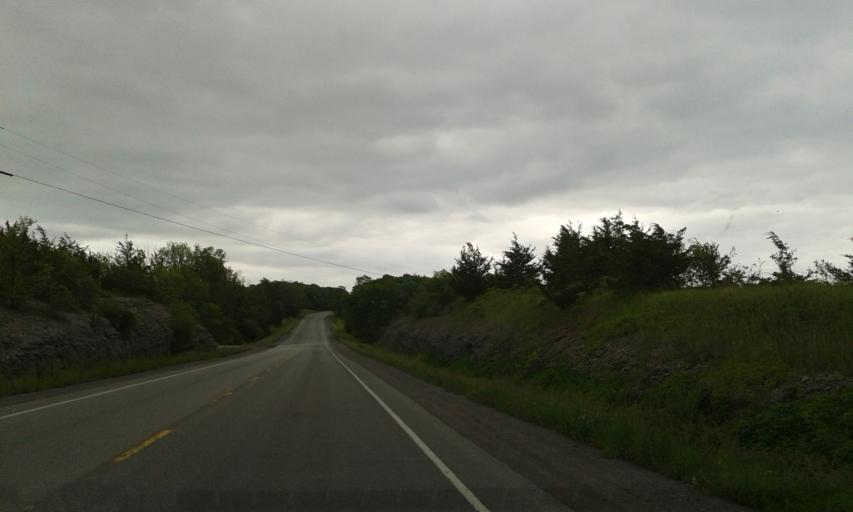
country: CA
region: Ontario
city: Quinte West
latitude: 43.9786
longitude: -77.5089
